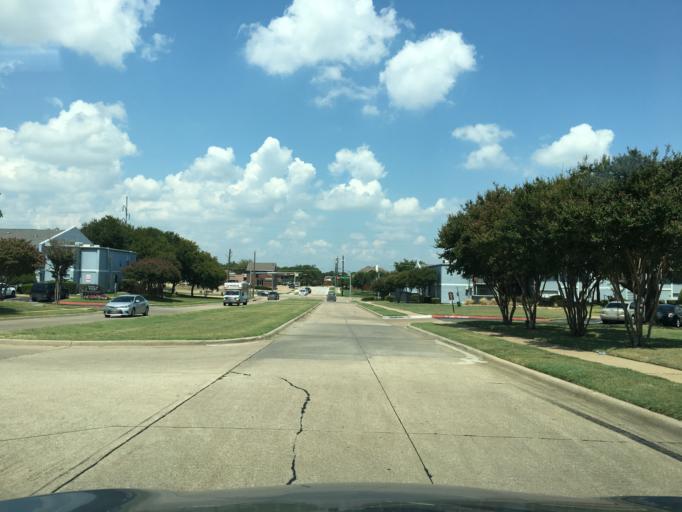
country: US
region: Texas
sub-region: Dallas County
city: Garland
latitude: 32.9436
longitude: -96.6534
